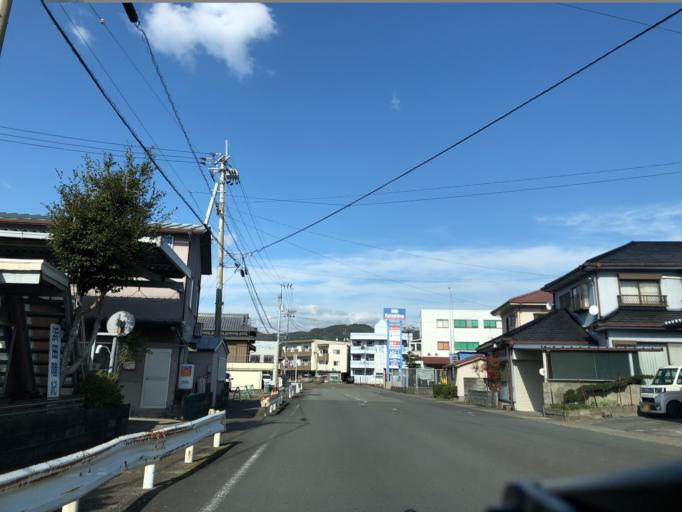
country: JP
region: Kochi
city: Sukumo
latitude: 32.9254
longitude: 132.7024
